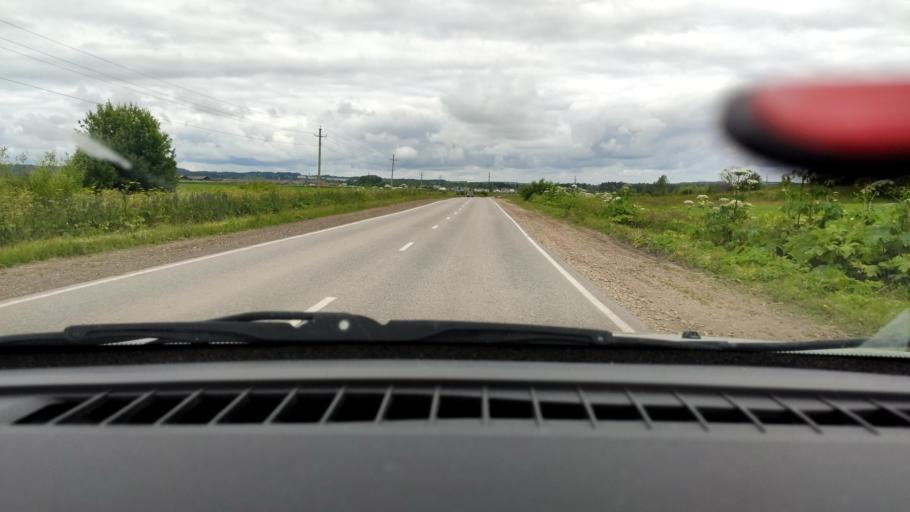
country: RU
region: Perm
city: Ust'-Kachka
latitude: 58.0723
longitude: 55.6243
